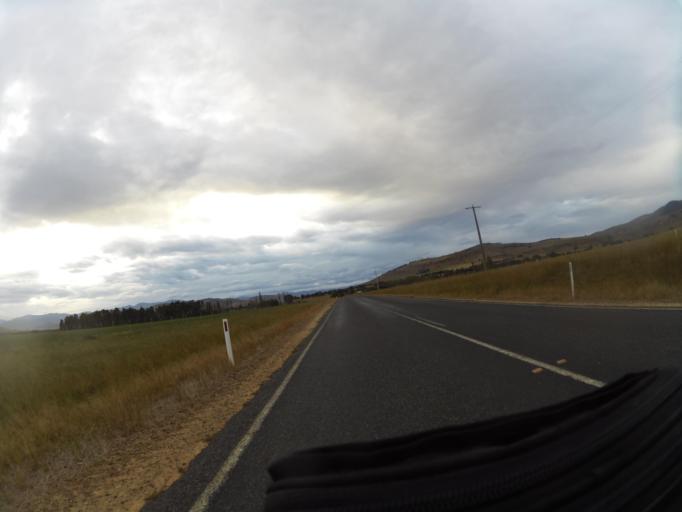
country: AU
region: New South Wales
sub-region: Greater Hume Shire
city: Holbrook
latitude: -36.0640
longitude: 147.9497
